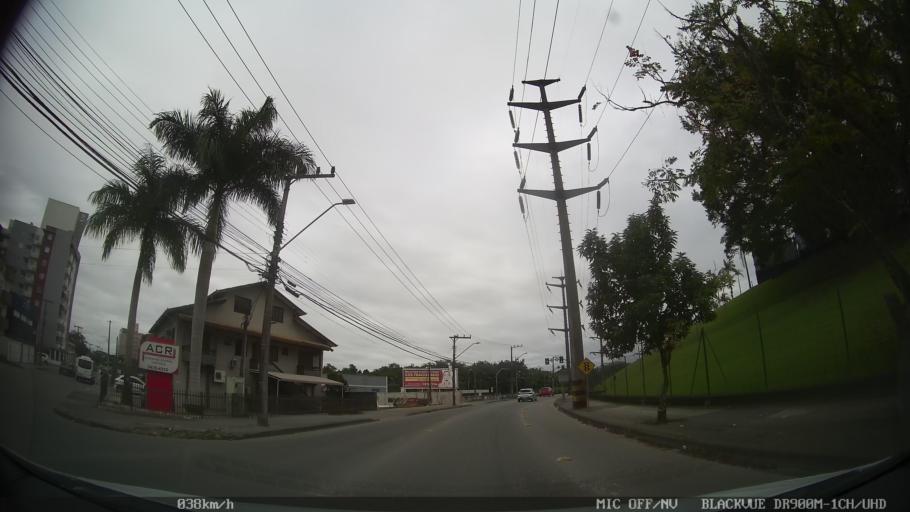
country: BR
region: Santa Catarina
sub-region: Joinville
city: Joinville
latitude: -26.2642
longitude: -48.8685
